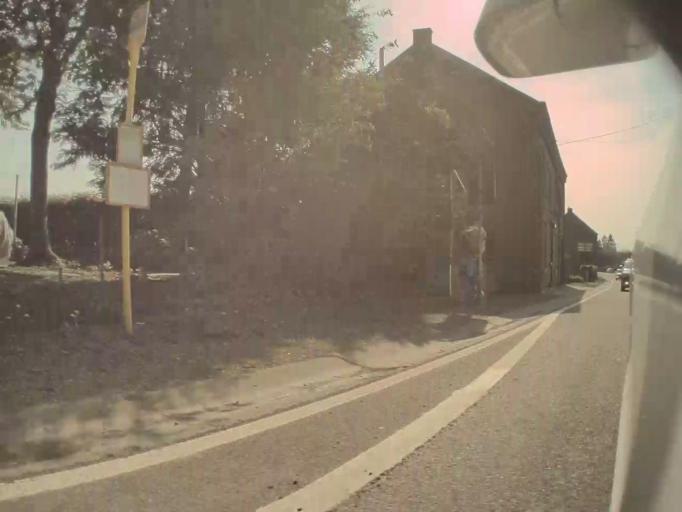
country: BE
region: Wallonia
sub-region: Province de Namur
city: Havelange
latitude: 50.3288
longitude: 5.2601
